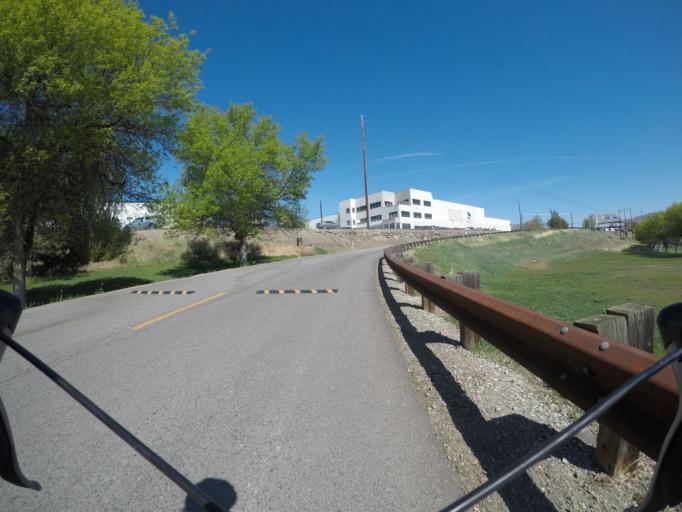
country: US
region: Washington
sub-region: Chelan County
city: Sunnyslope
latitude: 47.4607
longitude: -120.3301
